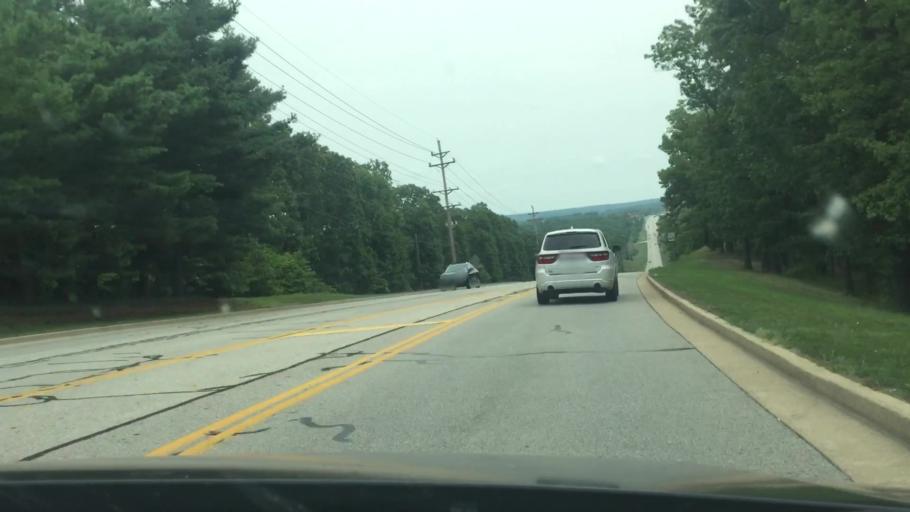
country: US
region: Missouri
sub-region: Miller County
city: Lake Ozark
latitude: 38.1923
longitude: -92.6648
